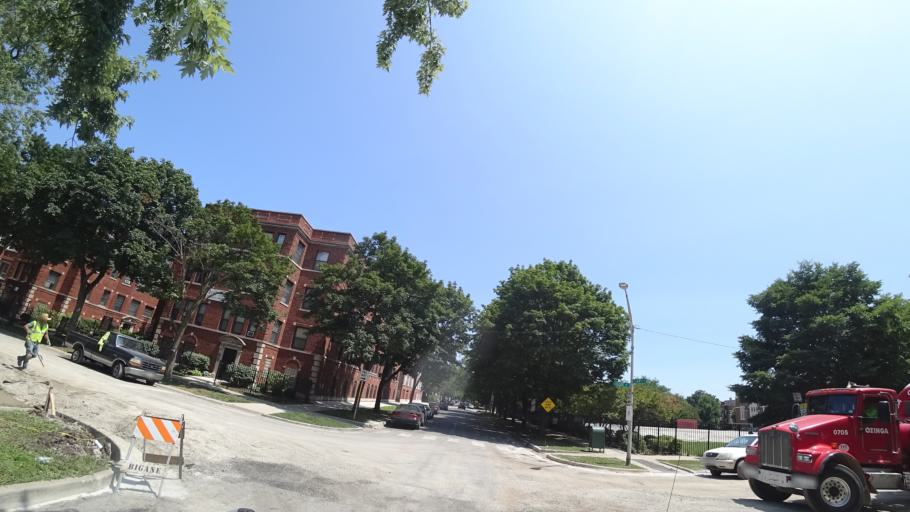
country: US
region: Illinois
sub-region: Cook County
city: Chicago
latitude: 41.7698
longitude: -87.5741
